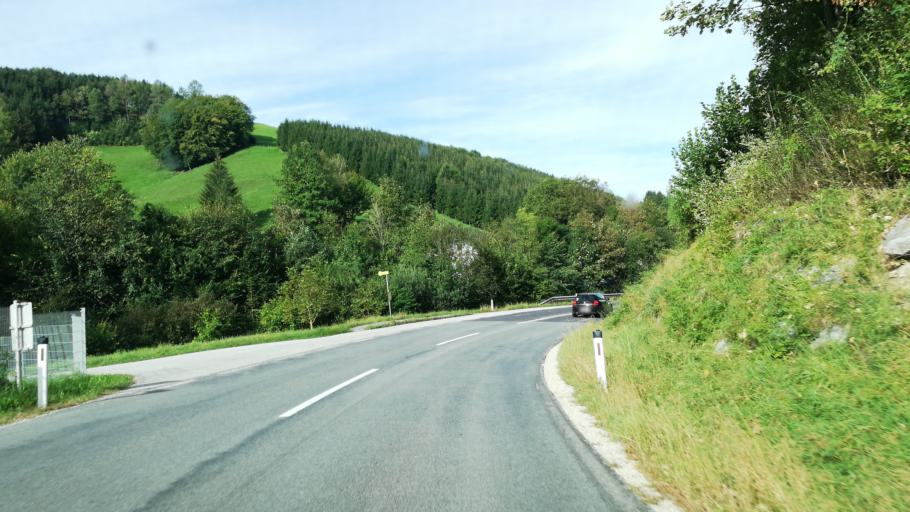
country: AT
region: Lower Austria
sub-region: Politischer Bezirk Amstetten
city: Behamberg
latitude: 47.9864
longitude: 14.5395
